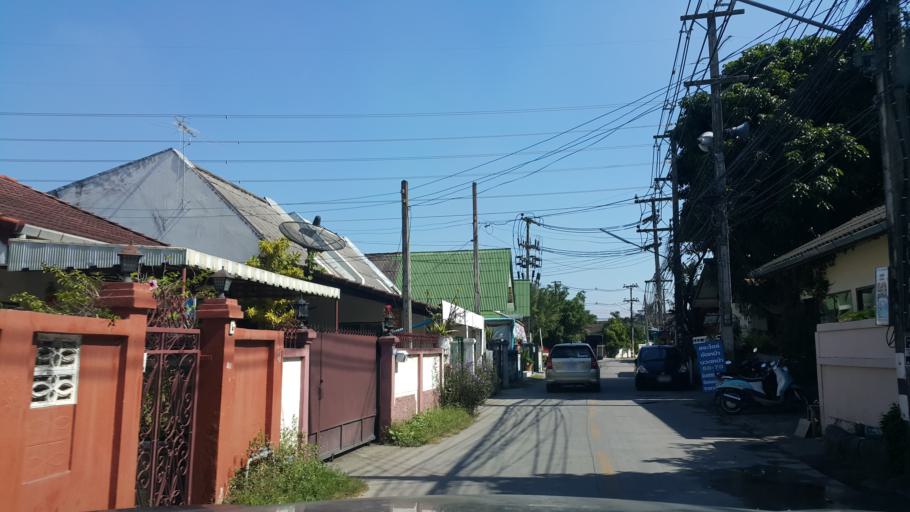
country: TH
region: Chiang Mai
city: Chiang Mai
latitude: 18.7666
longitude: 99.0075
